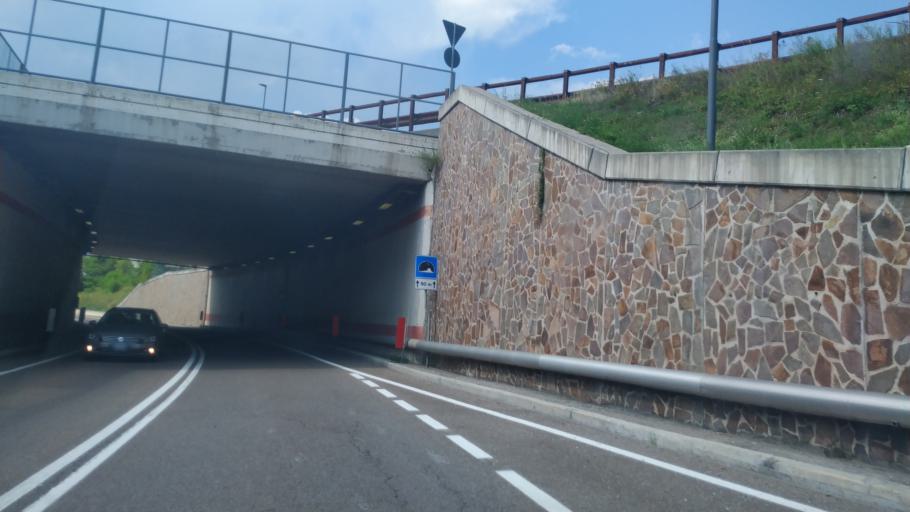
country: IT
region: Trentino-Alto Adige
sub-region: Provincia di Trento
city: Taio
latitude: 46.3124
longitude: 11.0701
